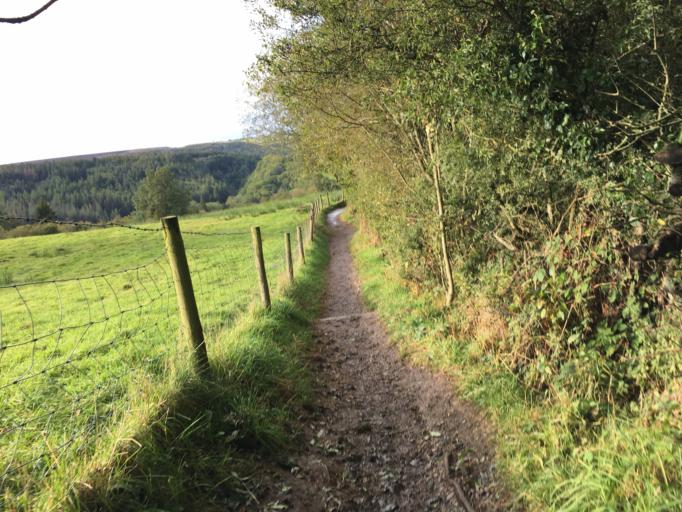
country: GB
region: England
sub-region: North Yorkshire
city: Sleights
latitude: 54.3962
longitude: -0.7274
